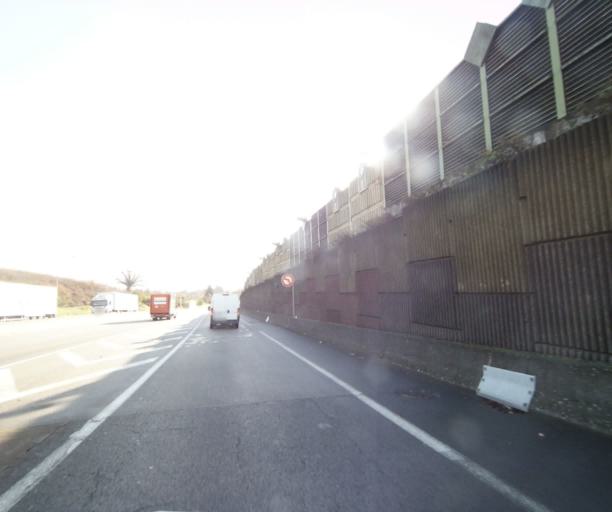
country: FR
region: Rhone-Alpes
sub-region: Departement de la Loire
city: Mably
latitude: 46.0620
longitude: 4.0643
